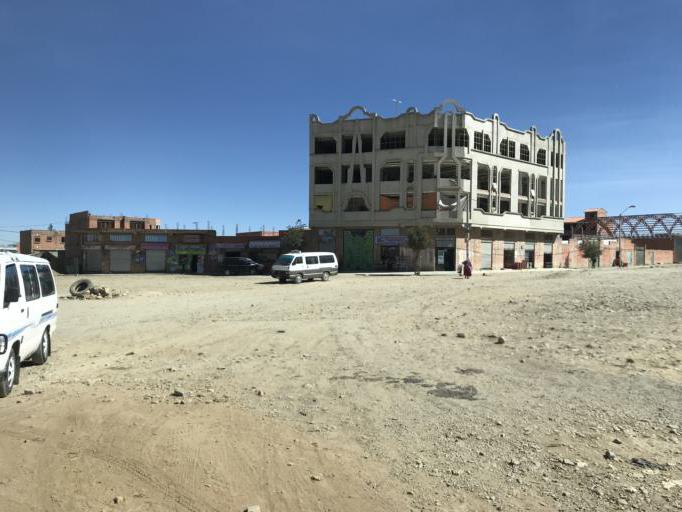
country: BO
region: La Paz
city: La Paz
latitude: -16.5014
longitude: -68.2405
